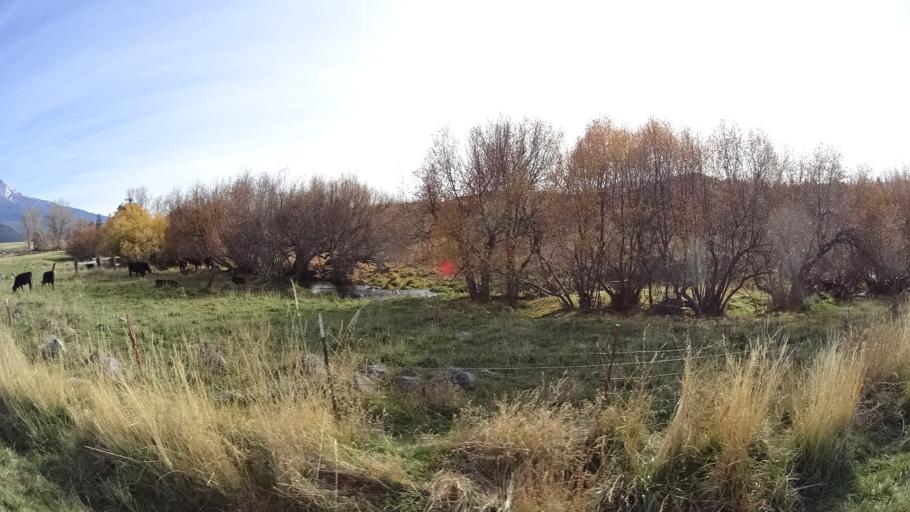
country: US
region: California
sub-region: Siskiyou County
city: Weed
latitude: 41.4651
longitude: -122.3900
